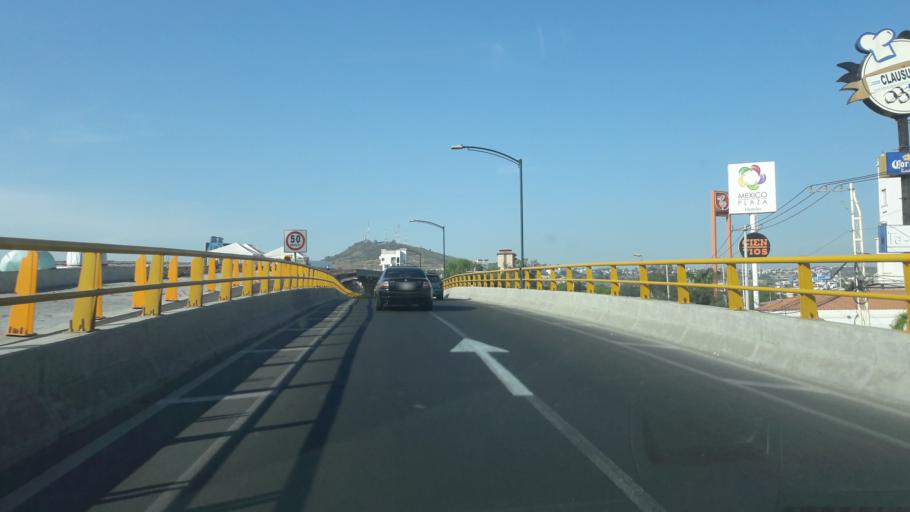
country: MX
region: Guanajuato
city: Leon
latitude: 21.1689
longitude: -101.6913
